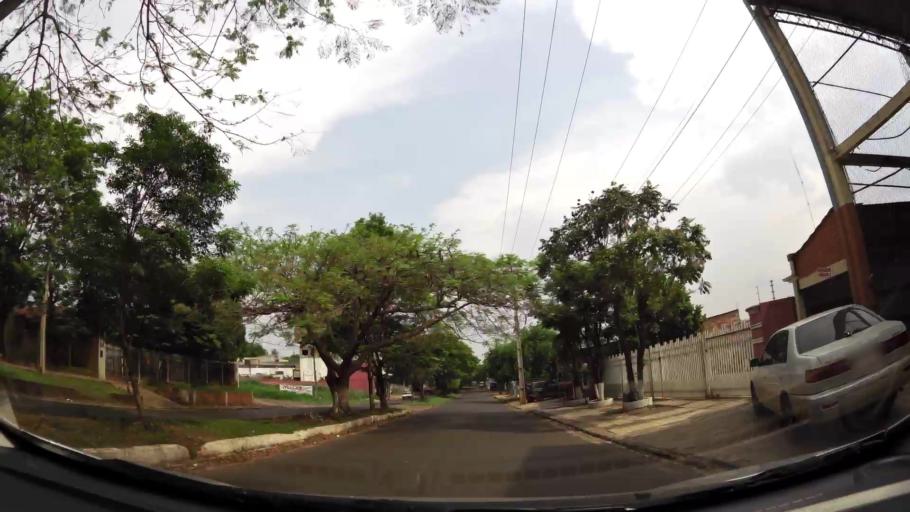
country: PY
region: Alto Parana
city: Presidente Franco
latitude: -25.5363
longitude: -54.6065
